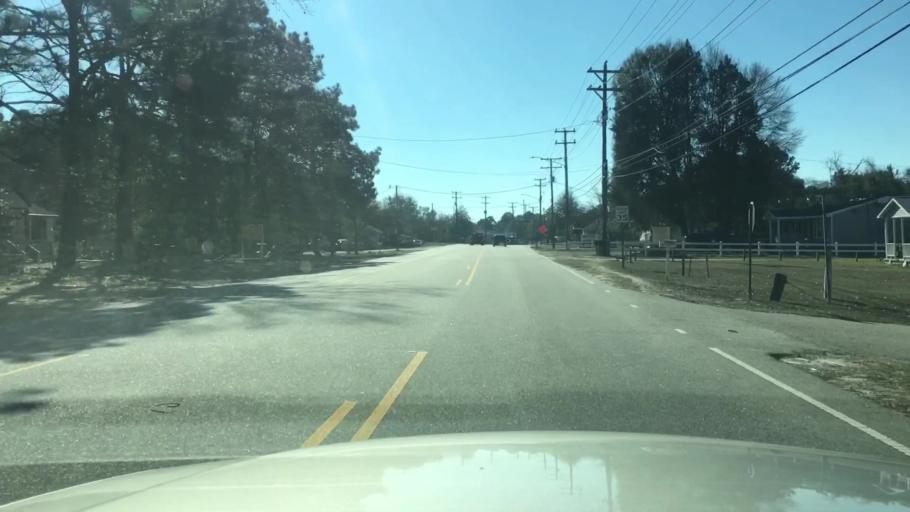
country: US
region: North Carolina
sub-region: Cumberland County
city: Hope Mills
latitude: 35.0176
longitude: -78.9352
